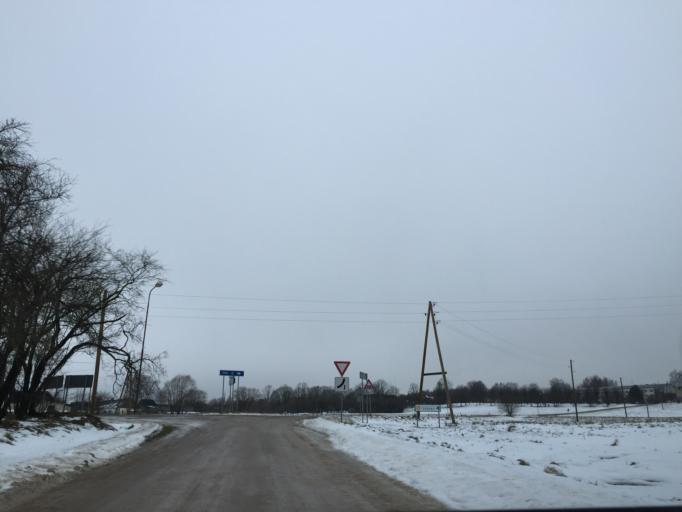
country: LV
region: Krimulda
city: Ragana
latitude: 57.1556
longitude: 24.7093
